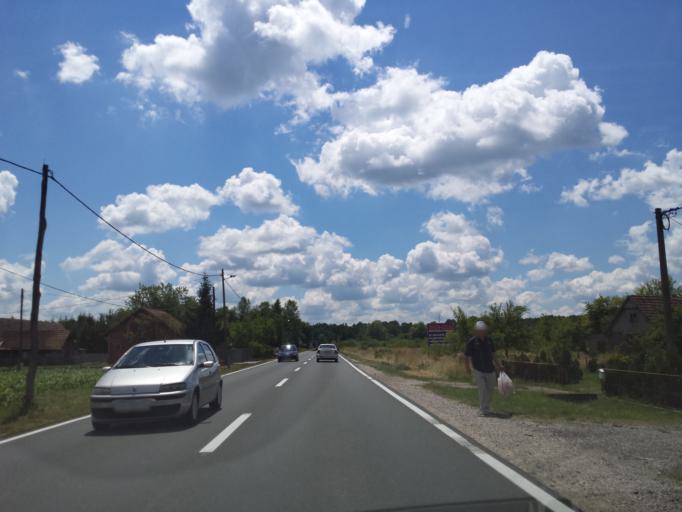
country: HR
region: Sisacko-Moslavacka
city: Lekenik
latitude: 45.5277
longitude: 16.2406
